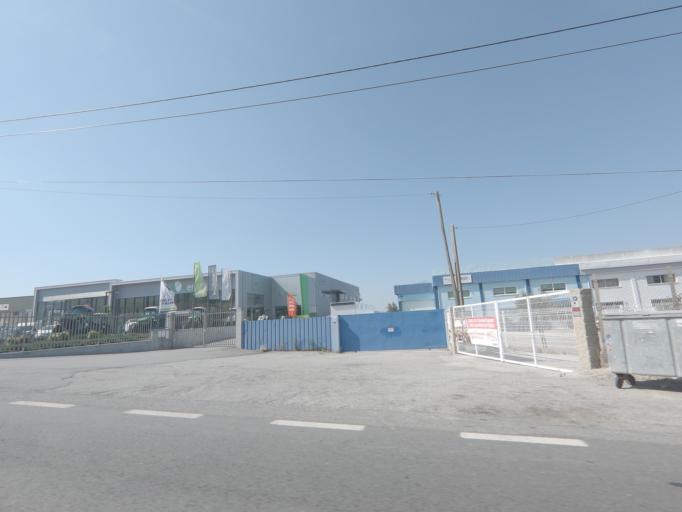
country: PT
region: Viseu
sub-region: Moimenta da Beira
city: Moimenta da Beira
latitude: 40.9842
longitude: -7.6340
